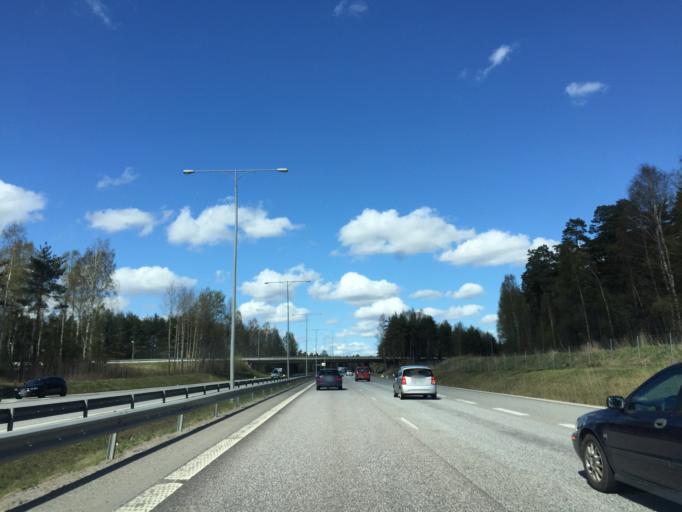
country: SE
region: OErebro
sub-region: Orebro Kommun
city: Orebro
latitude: 59.2412
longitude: 15.1456
